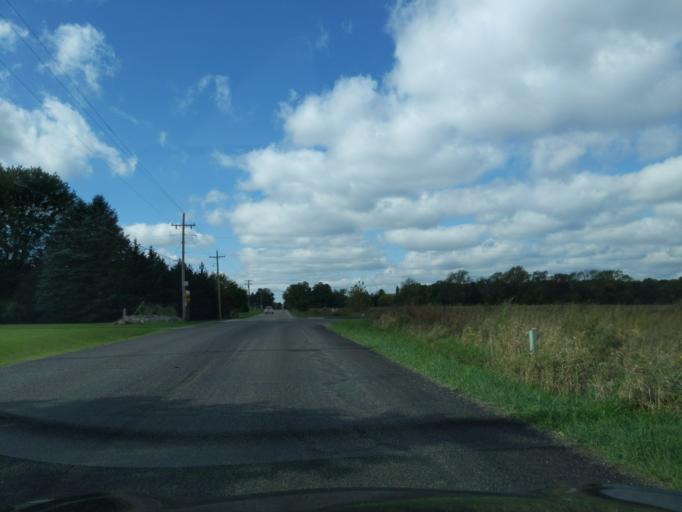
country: US
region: Michigan
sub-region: Eaton County
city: Potterville
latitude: 42.5677
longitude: -84.7382
